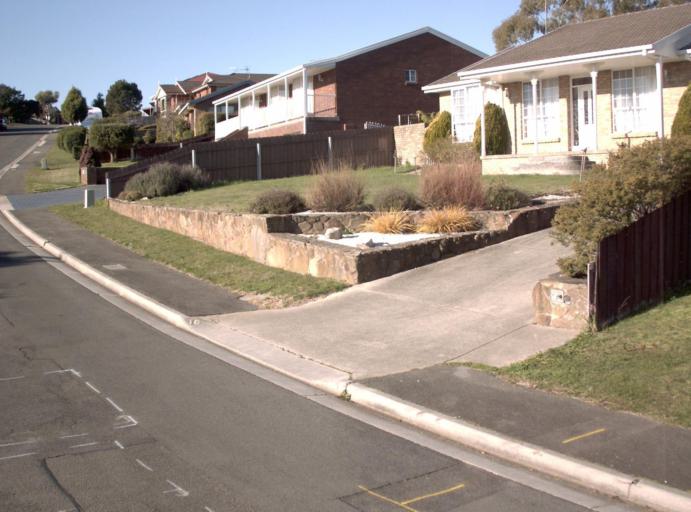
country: AU
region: Tasmania
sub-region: Launceston
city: Summerhill
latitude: -41.4632
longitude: 147.1257
